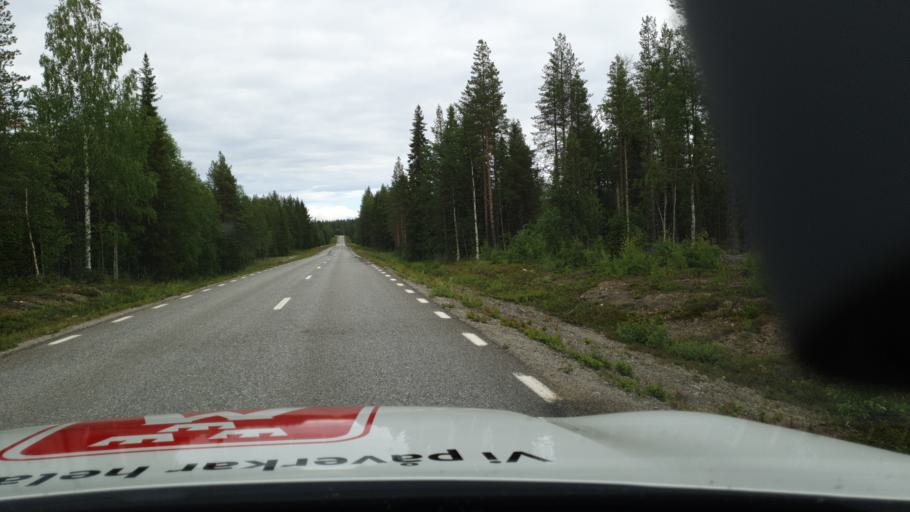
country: SE
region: Vaesterbotten
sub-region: Lycksele Kommun
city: Soderfors
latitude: 64.6188
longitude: 18.1553
